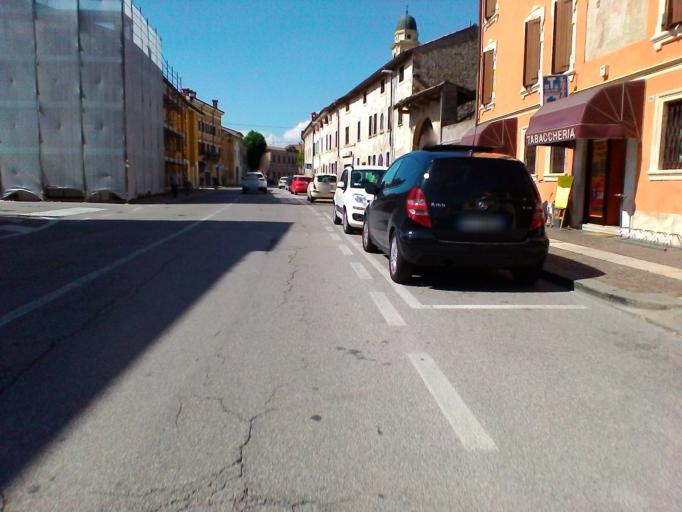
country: IT
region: Veneto
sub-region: Provincia di Verona
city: Povegliano Veronese
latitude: 45.3458
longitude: 10.8816
